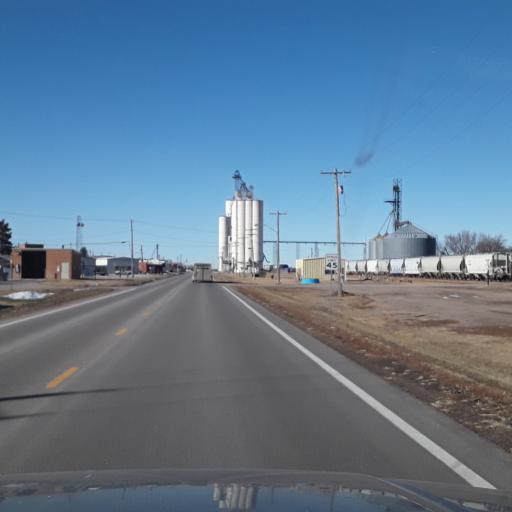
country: US
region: Nebraska
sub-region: Gosper County
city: Elwood
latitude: 40.5267
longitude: -99.6301
